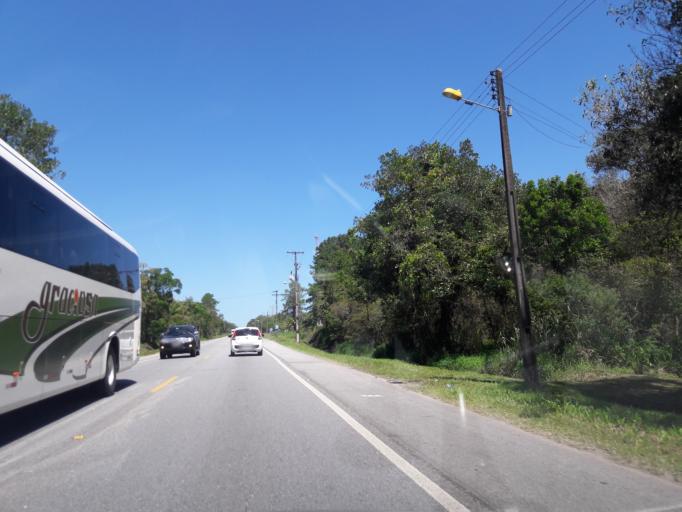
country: BR
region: Parana
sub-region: Pontal Do Parana
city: Pontal do Parana
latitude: -25.6378
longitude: -48.5351
